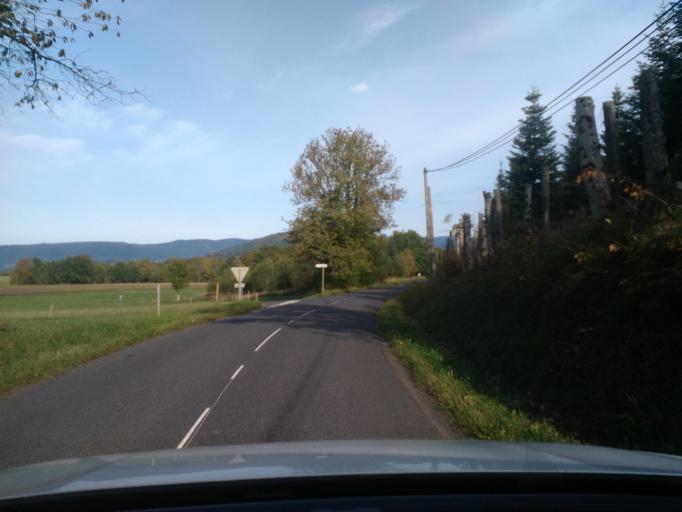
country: FR
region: Lorraine
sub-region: Departement des Vosges
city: Senones
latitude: 48.3486
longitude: 7.0202
